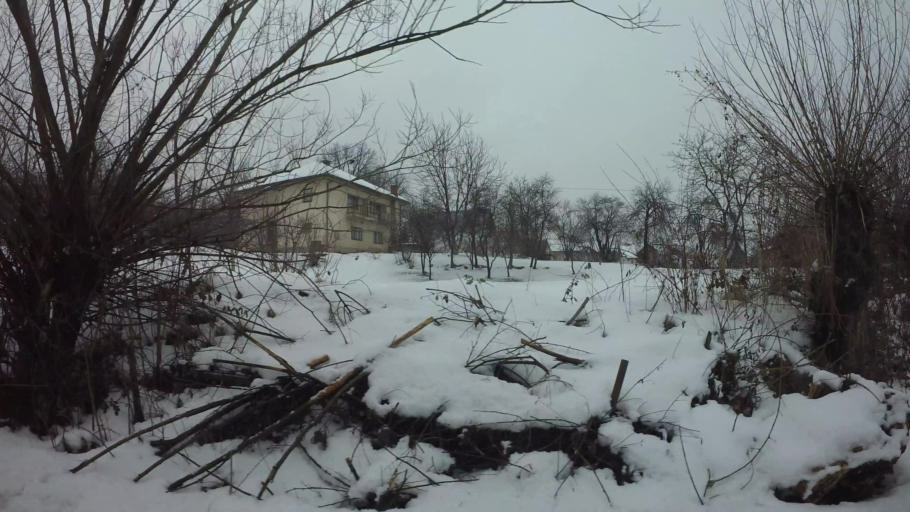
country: BA
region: Federation of Bosnia and Herzegovina
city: Hadzici
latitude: 43.8423
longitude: 18.2686
